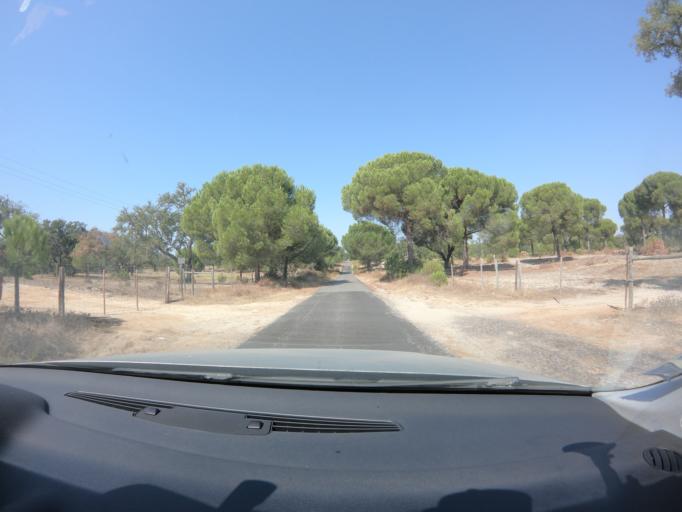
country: PT
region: Setubal
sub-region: Alcacer do Sal
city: Alcacer do Sal
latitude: 38.2630
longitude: -8.3116
